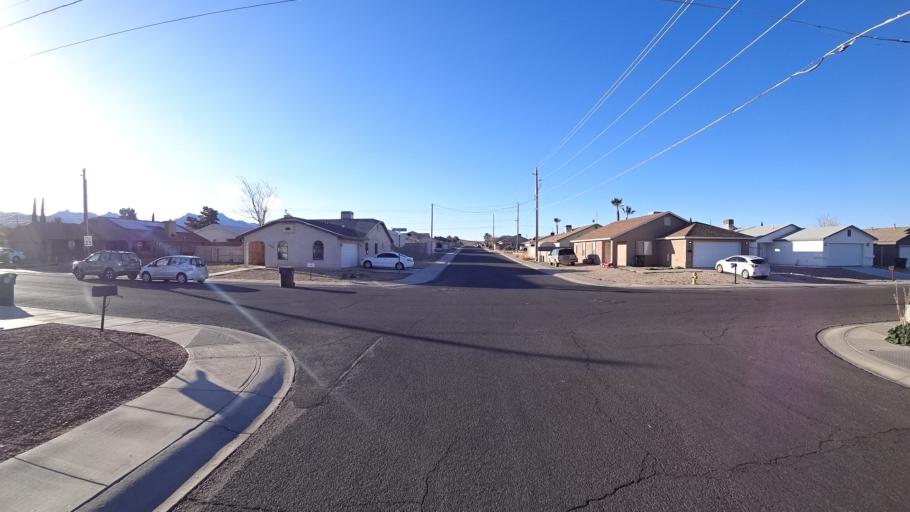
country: US
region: Arizona
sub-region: Mohave County
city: Kingman
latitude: 35.1994
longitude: -114.0136
